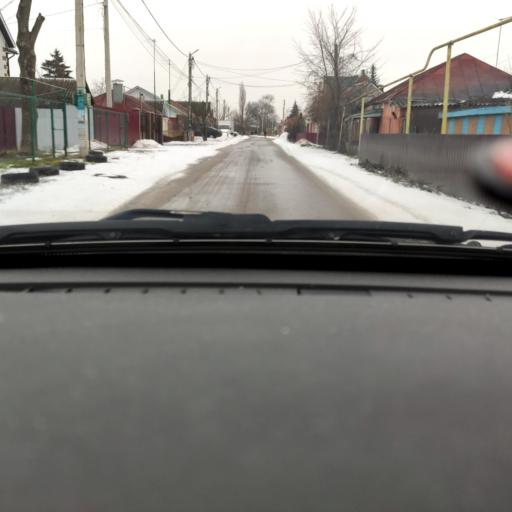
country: RU
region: Voronezj
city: Novaya Usman'
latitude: 51.6413
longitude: 39.4140
